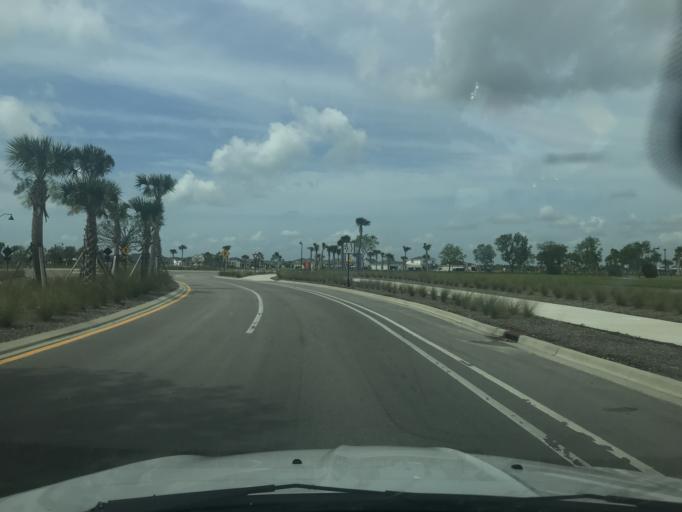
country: US
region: Florida
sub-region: Lee County
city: Olga
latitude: 26.7833
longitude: -81.7407
